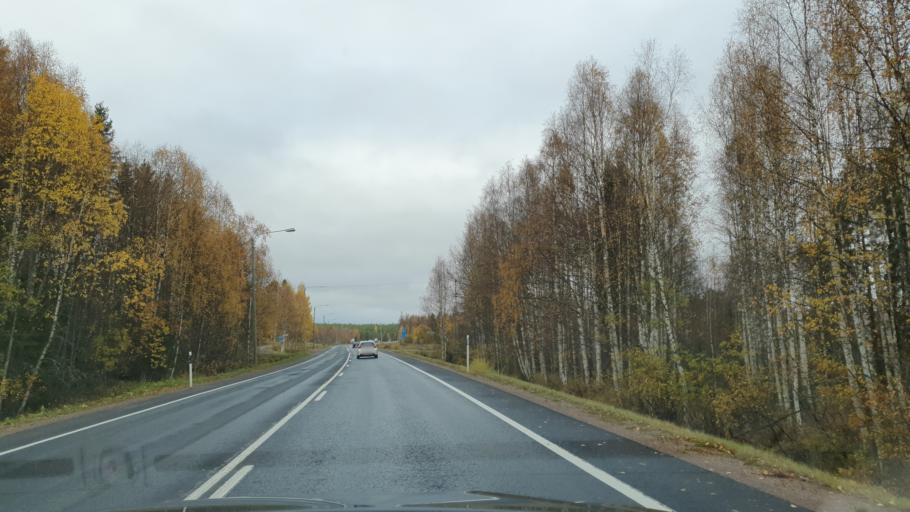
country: FI
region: Lapland
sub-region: Rovaniemi
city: Rovaniemi
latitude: 66.6344
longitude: 25.5082
